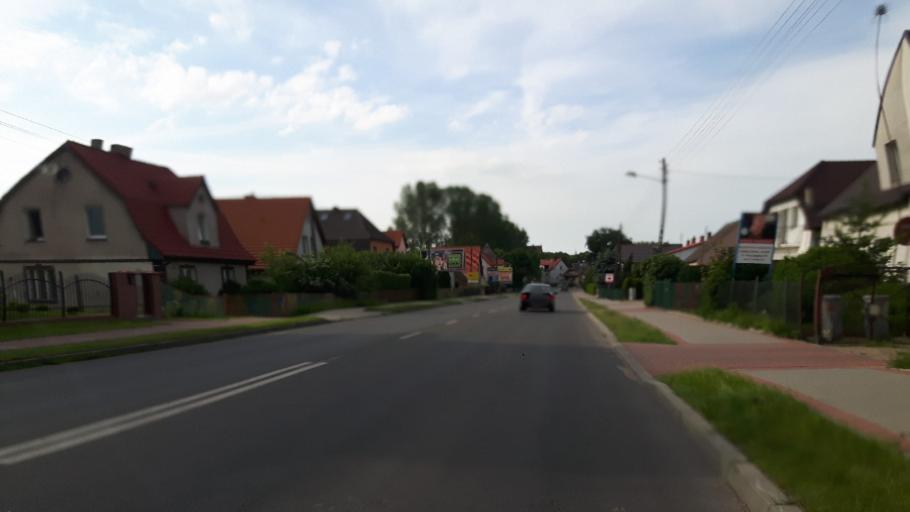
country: PL
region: West Pomeranian Voivodeship
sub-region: Powiat gryficki
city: Gryfice
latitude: 53.9073
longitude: 15.2009
